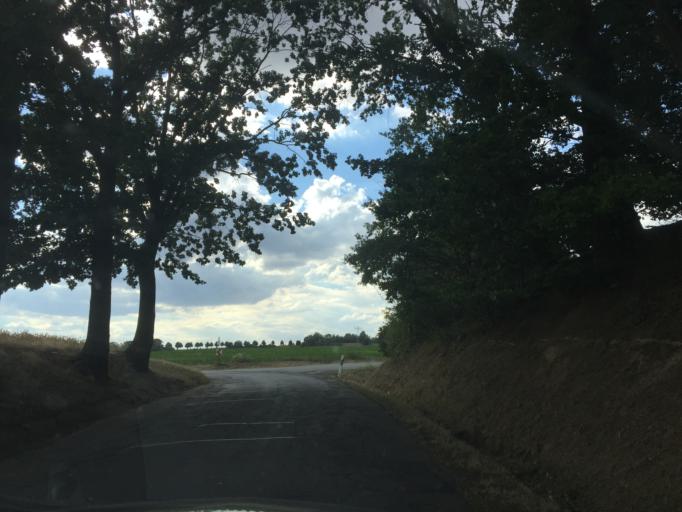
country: DE
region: Thuringia
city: Altenburg
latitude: 50.9603
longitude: 12.4413
